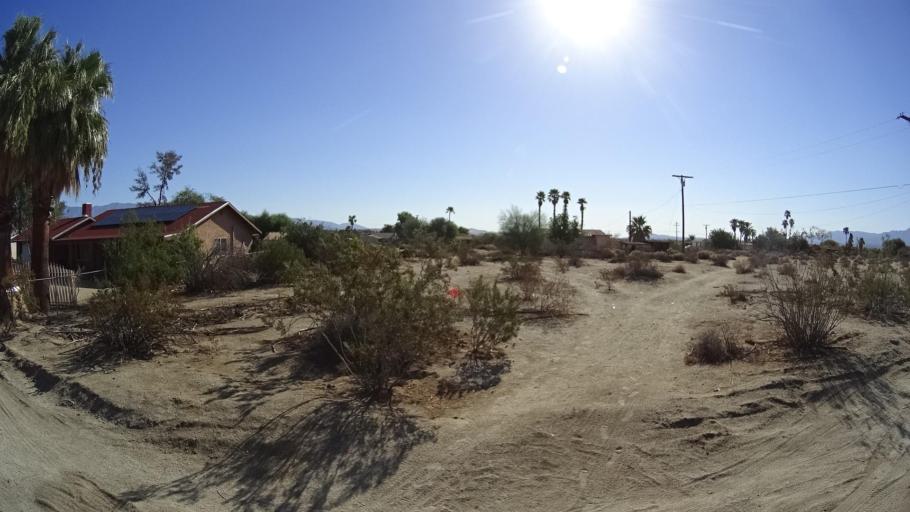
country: US
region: California
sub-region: San Diego County
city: Borrego Springs
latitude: 33.2548
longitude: -116.3723
